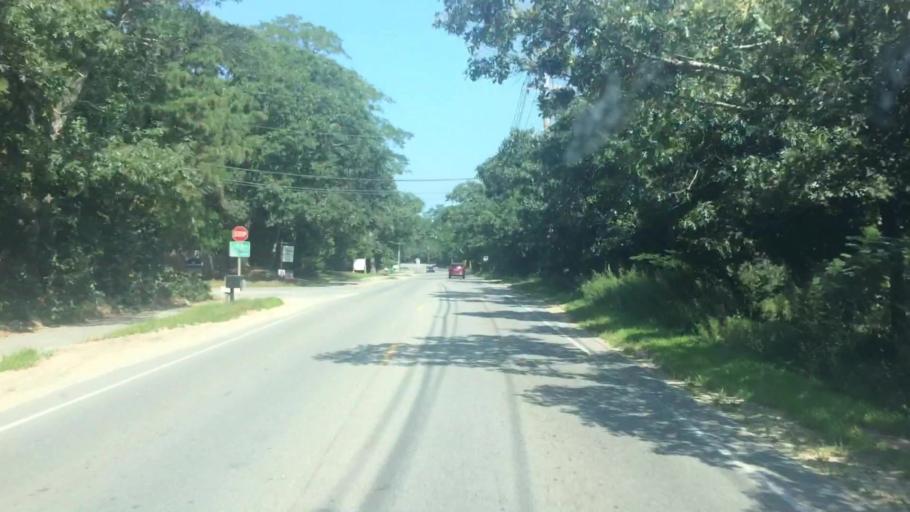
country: US
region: Massachusetts
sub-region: Dukes County
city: Vineyard Haven
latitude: 41.4368
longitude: -70.6080
